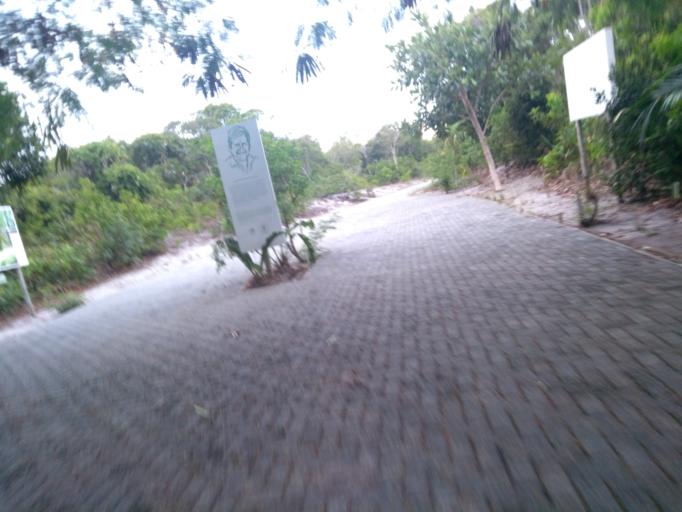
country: BR
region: Bahia
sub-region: Mata De Sao Joao
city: Mata de Sao Joao
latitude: -12.5750
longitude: -38.0093
